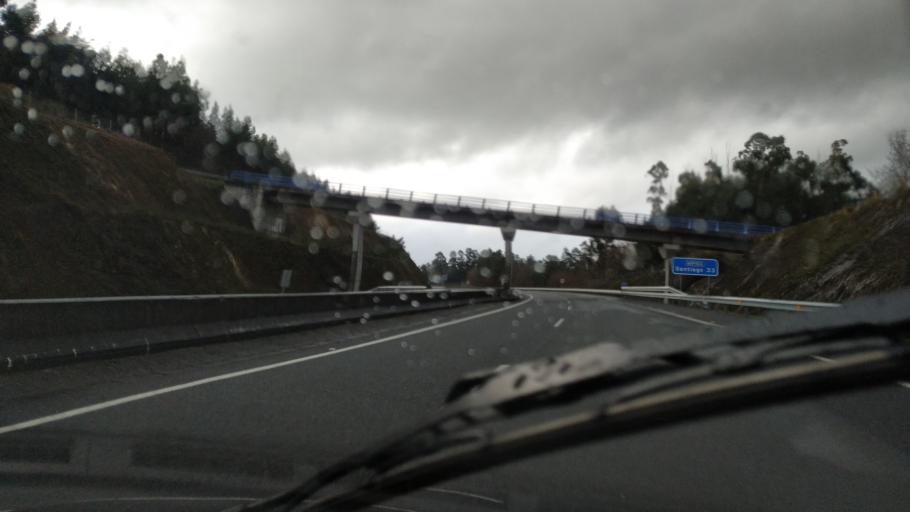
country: ES
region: Galicia
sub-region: Provincia de Pontevedra
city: Silleda
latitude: 42.7156
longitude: -8.2401
